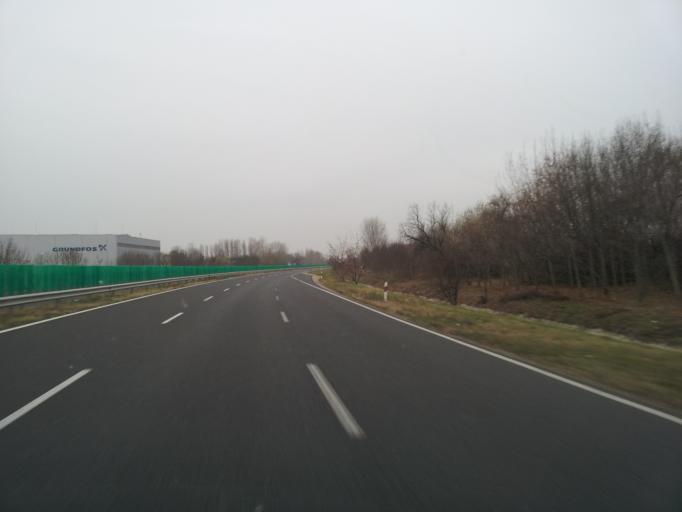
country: HU
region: Fejer
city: Szekesfehervar
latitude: 47.1479
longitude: 18.4196
